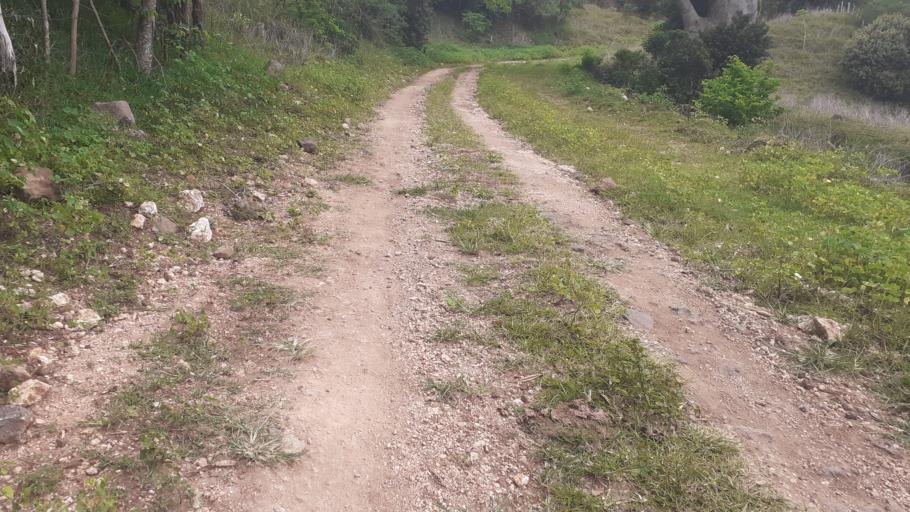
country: VU
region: Tafea
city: Isangel
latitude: -18.8189
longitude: 169.0244
